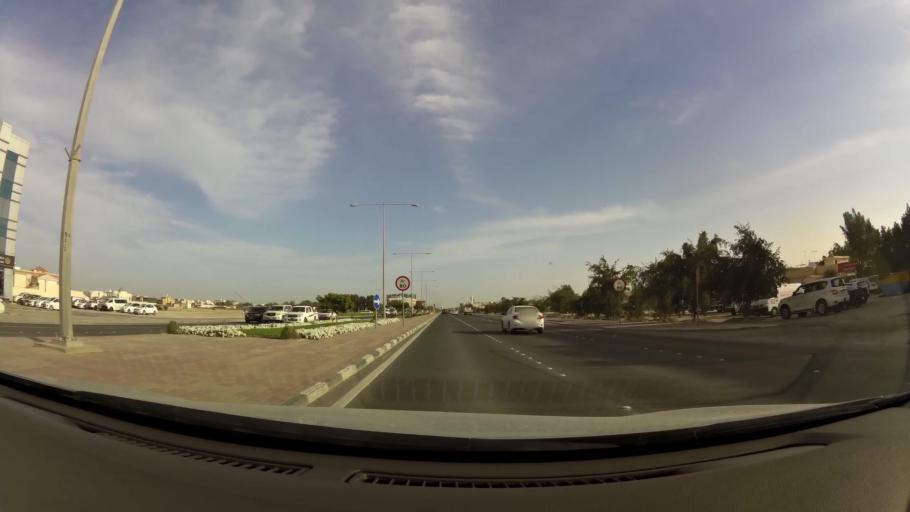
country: QA
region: Al Wakrah
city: Al Wakrah
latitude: 25.1859
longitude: 51.6000
